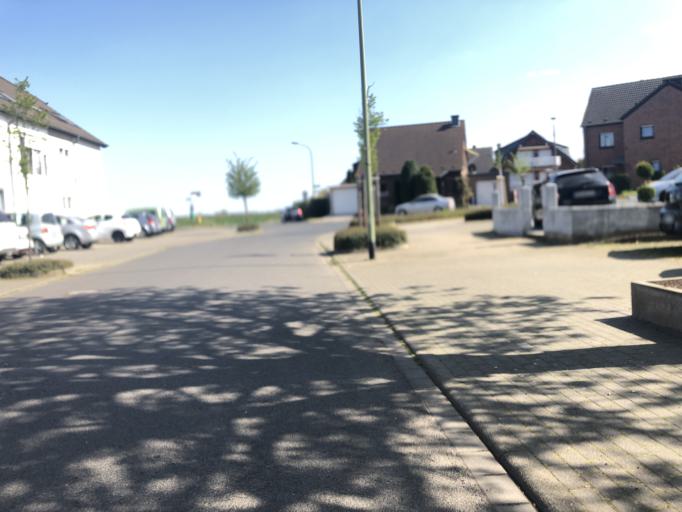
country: DE
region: North Rhine-Westphalia
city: Zulpich
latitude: 50.6936
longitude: 6.6591
